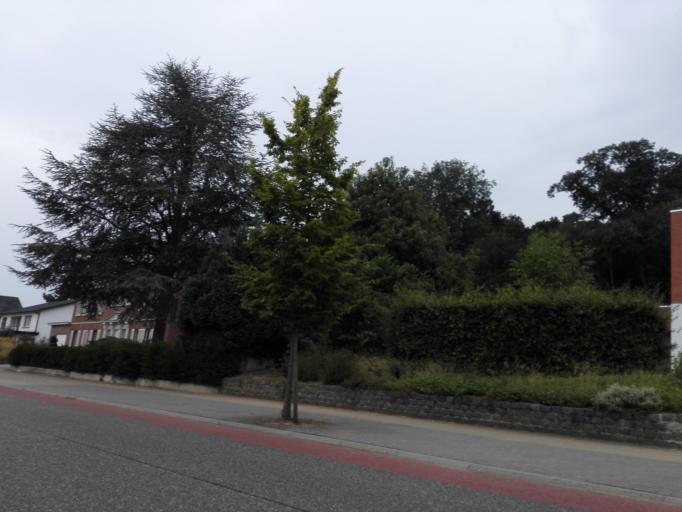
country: BE
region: Flanders
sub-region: Provincie Vlaams-Brabant
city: Holsbeek
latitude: 50.8930
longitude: 4.7684
